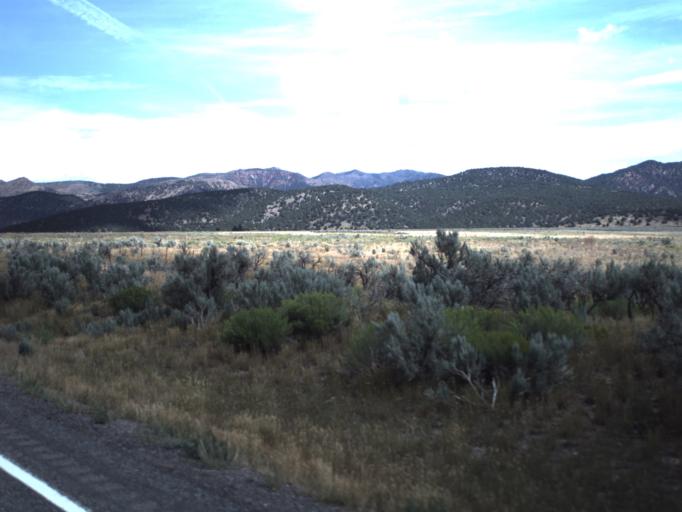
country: US
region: Utah
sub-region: Utah County
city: Woodland Hills
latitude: 39.8395
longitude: -111.5130
